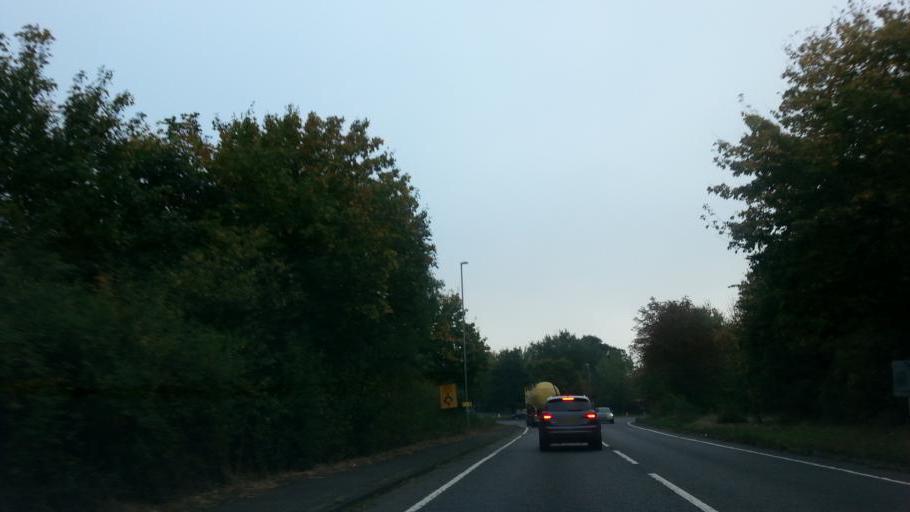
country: GB
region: England
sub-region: Northamptonshire
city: Oundle
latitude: 52.4893
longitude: -0.4582
